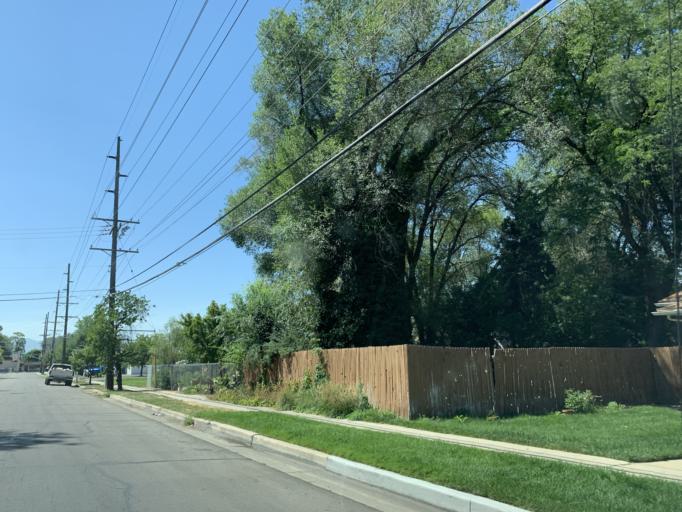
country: US
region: Utah
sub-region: Utah County
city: Provo
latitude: 40.2317
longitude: -111.6466
